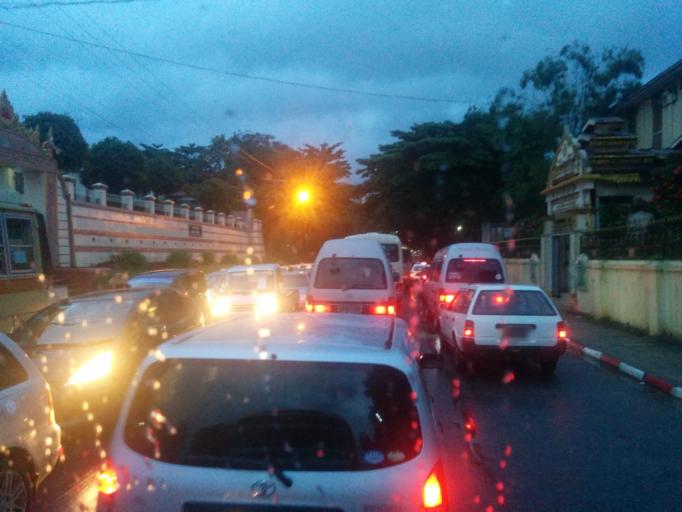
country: MM
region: Yangon
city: Yangon
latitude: 16.8039
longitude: 96.1286
